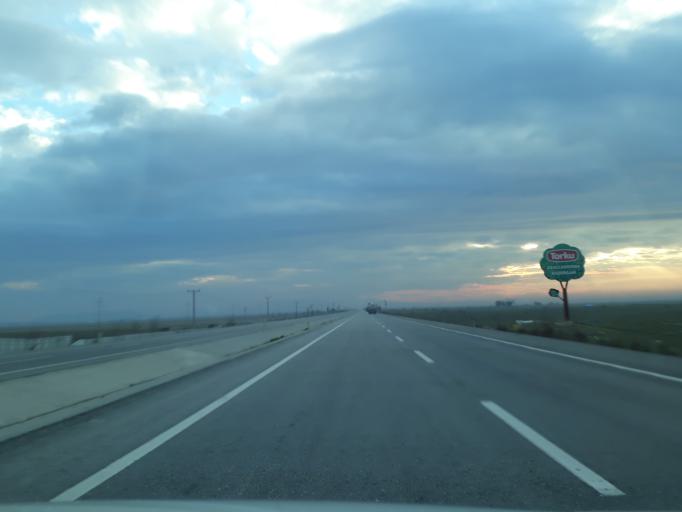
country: TR
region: Konya
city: Hotamis
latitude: 37.7107
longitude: 33.2853
